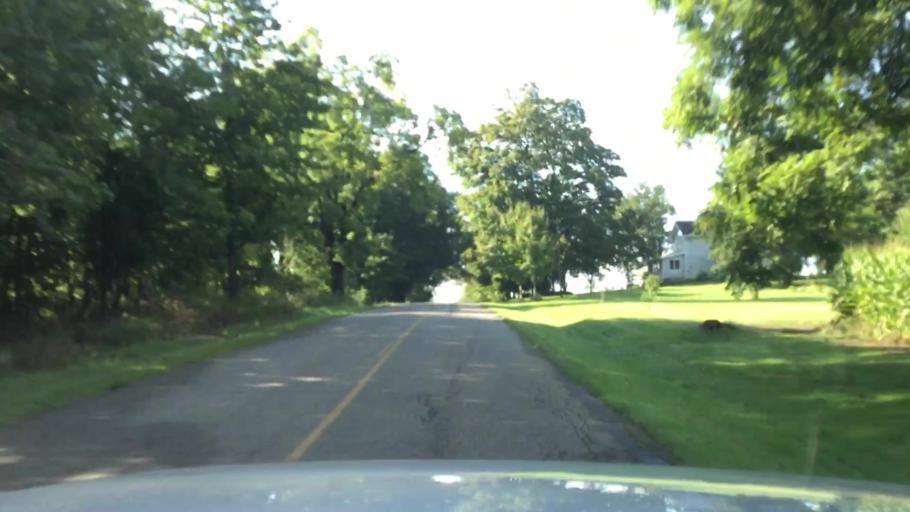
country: US
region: Michigan
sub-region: Lenawee County
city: Hudson
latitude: 41.9218
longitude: -84.4205
